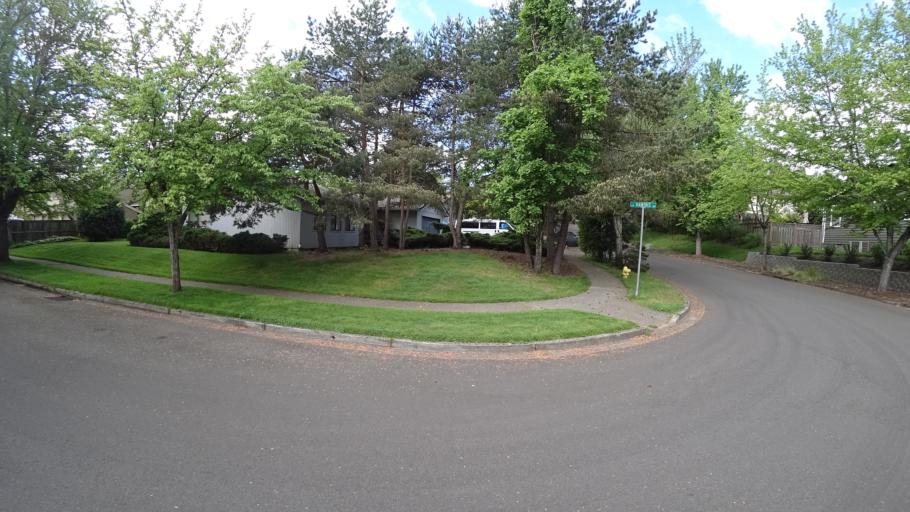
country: US
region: Oregon
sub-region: Washington County
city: Beaverton
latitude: 45.4641
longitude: -122.8063
